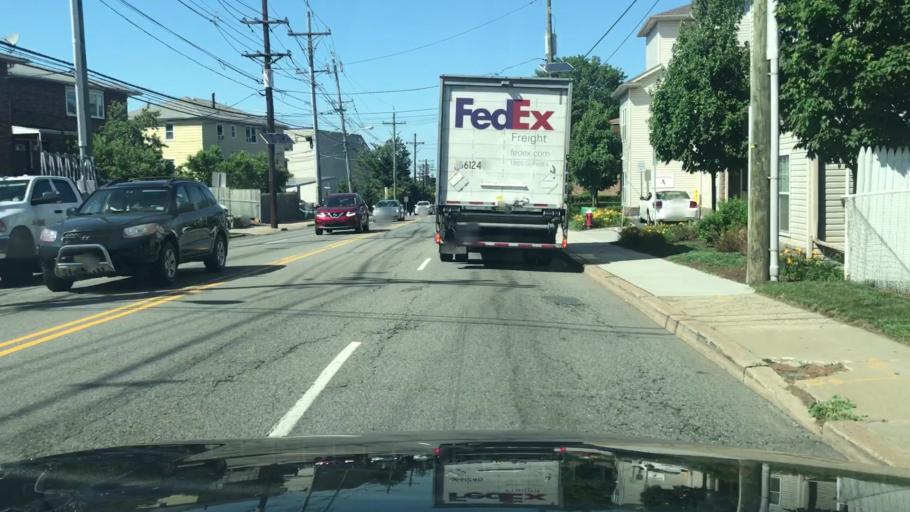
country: US
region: New Jersey
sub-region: Hudson County
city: Secaucus
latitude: 40.7863
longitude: -74.0554
